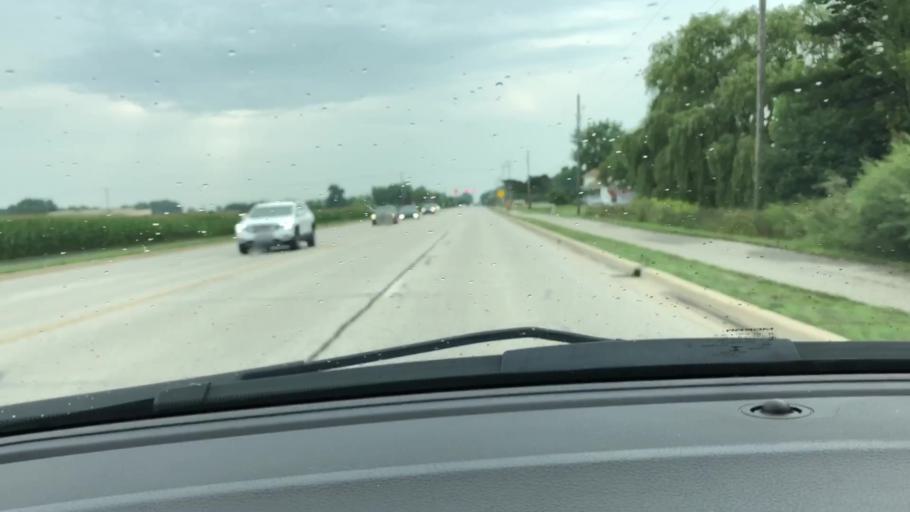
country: US
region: Michigan
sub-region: Saginaw County
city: Shields
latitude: 43.4806
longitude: -84.0115
